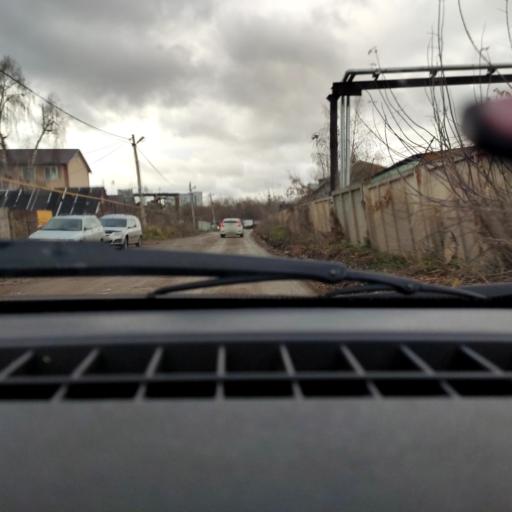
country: RU
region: Bashkortostan
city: Ufa
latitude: 54.7995
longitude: 56.1596
